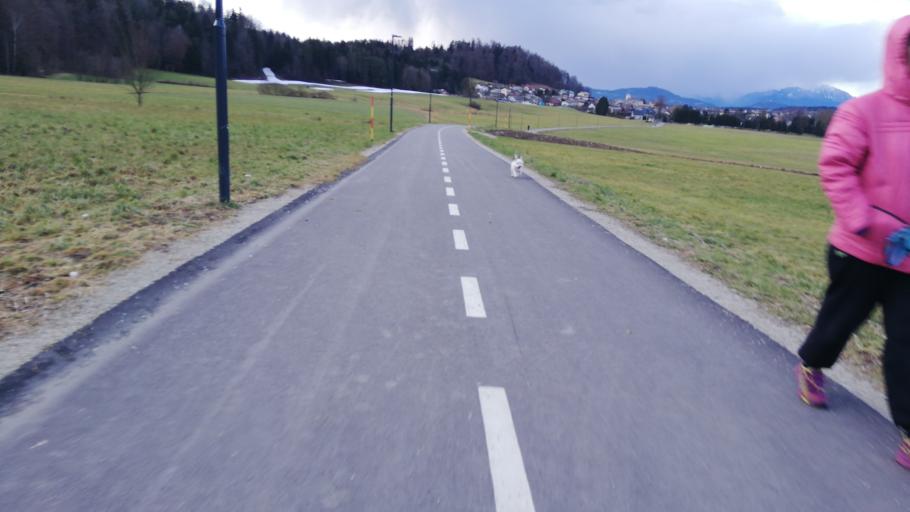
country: SI
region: Medvode
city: Medvode
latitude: 46.1247
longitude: 14.4189
